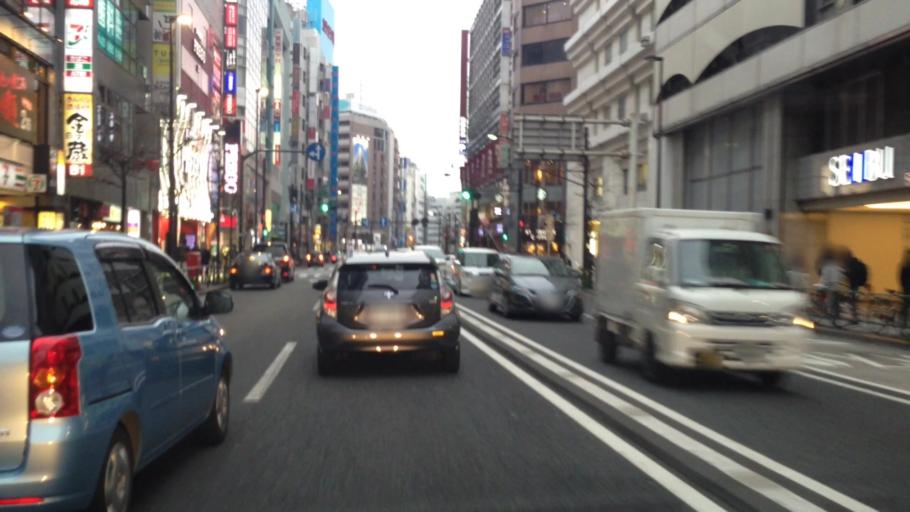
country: JP
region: Tokyo
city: Tokyo
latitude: 35.7287
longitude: 139.7121
